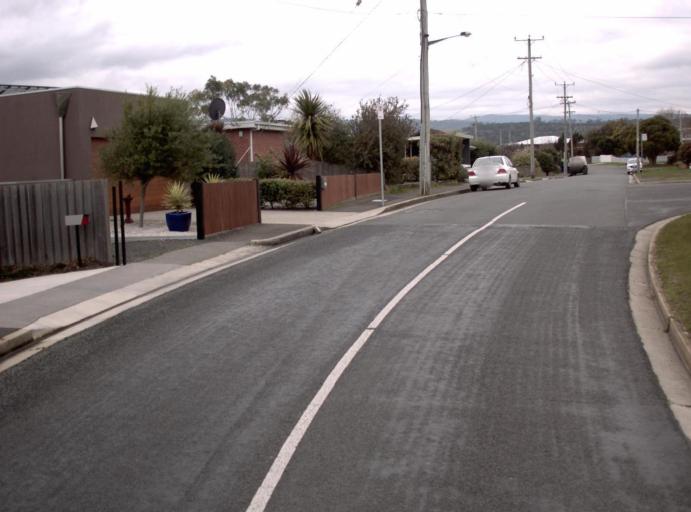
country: AU
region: Tasmania
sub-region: Launceston
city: Newstead
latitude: -41.4495
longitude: 147.1757
